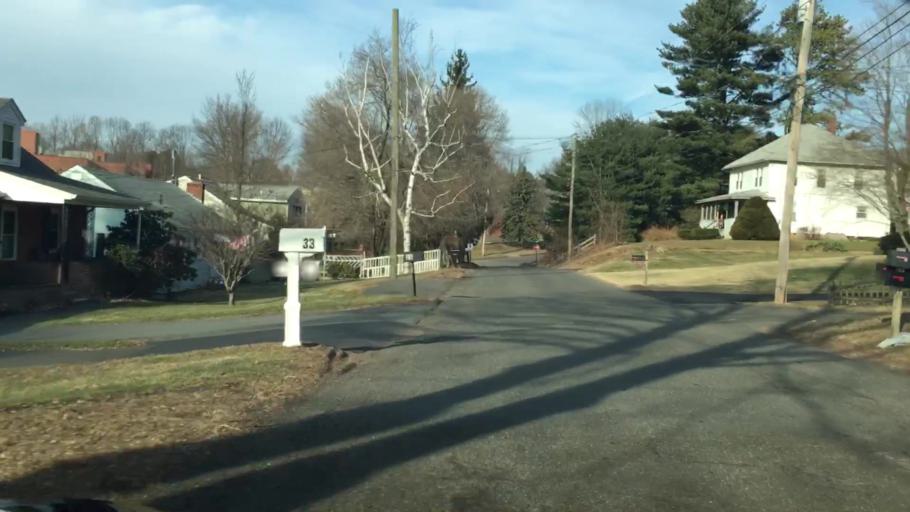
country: US
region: Connecticut
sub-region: New Haven County
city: Meriden
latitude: 41.5248
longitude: -72.7510
